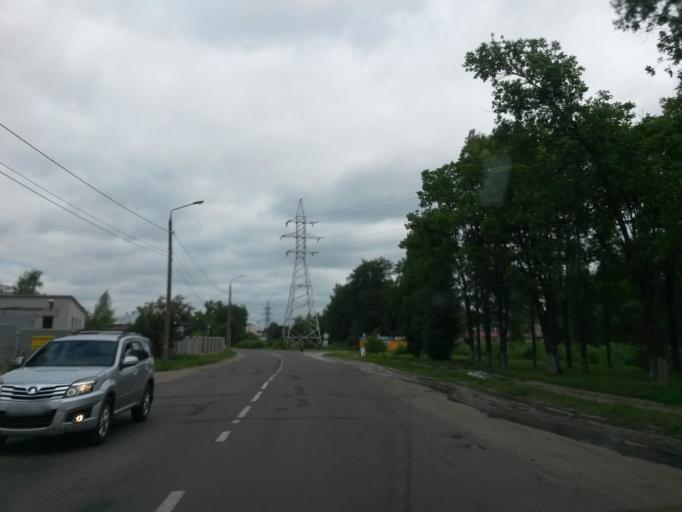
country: RU
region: Jaroslavl
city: Yaroslavl
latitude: 57.5863
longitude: 39.8756
